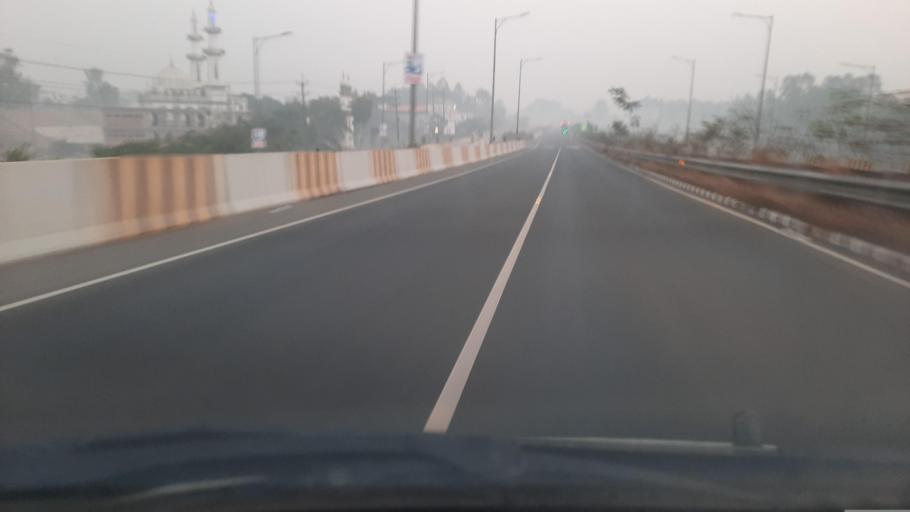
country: BD
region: Dhaka
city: Dohar
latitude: 23.5441
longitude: 90.2969
